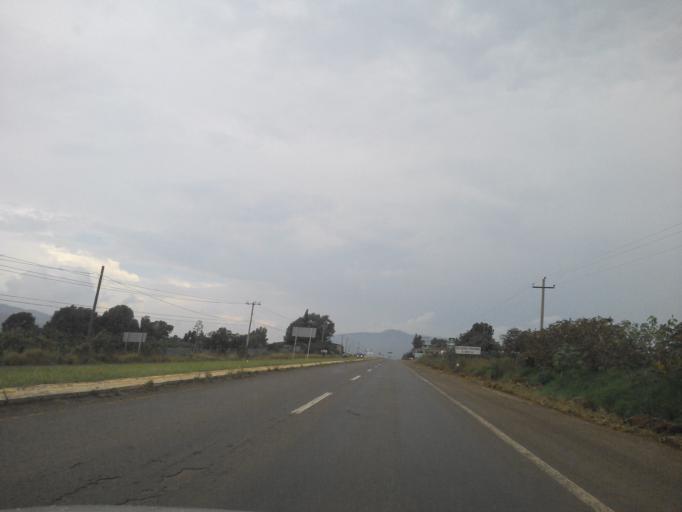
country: MX
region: Jalisco
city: San Jose de Gracia
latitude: 20.7382
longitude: -102.5126
